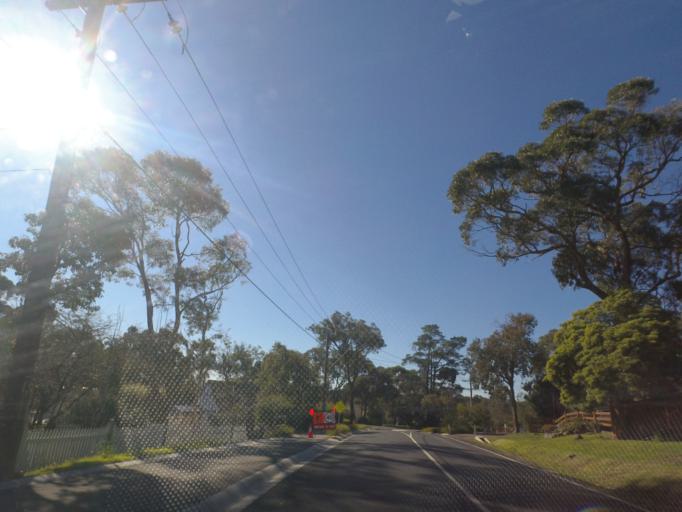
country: AU
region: Victoria
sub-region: Manningham
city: Warrandyte
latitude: -37.7366
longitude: 145.2711
